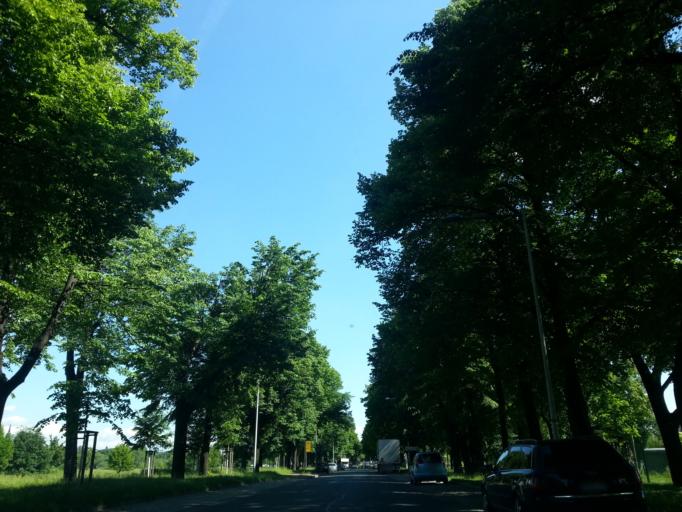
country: DE
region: Saxony
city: Dresden
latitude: 51.0660
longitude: 13.7249
